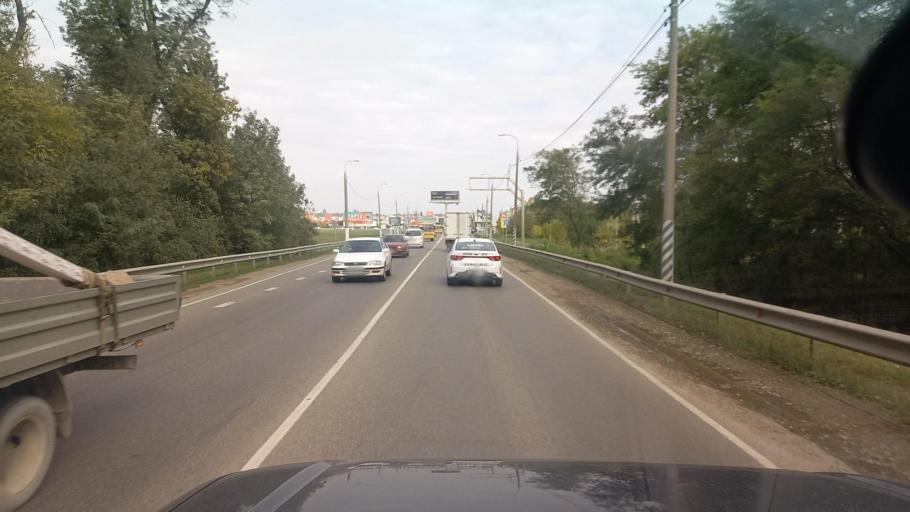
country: RU
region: Krasnodarskiy
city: Krasnodar
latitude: 45.1095
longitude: 38.9219
